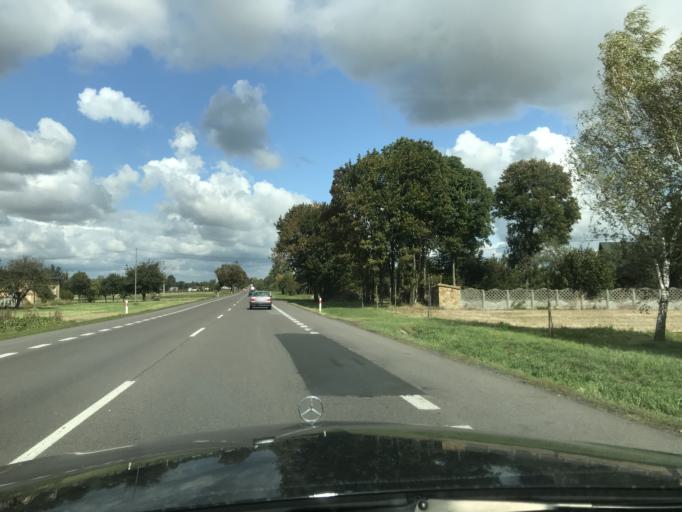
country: PL
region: Lublin Voivodeship
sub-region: Powiat krasnicki
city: Wilkolaz
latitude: 51.0479
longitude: 22.3808
